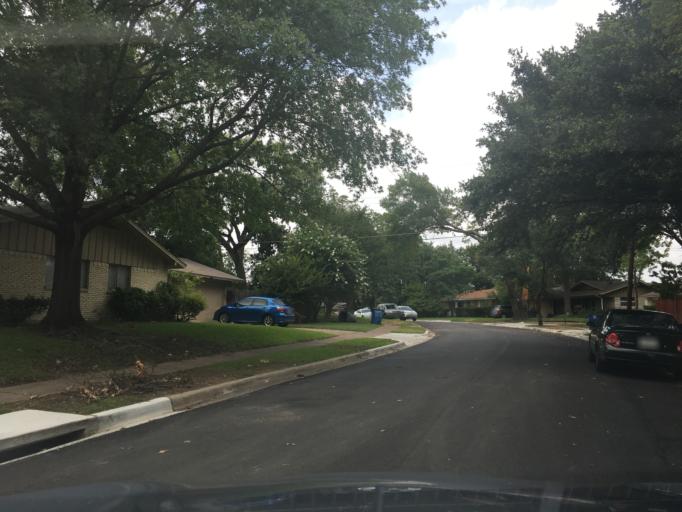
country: US
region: Texas
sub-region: Dallas County
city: Richardson
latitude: 32.9356
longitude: -96.7624
